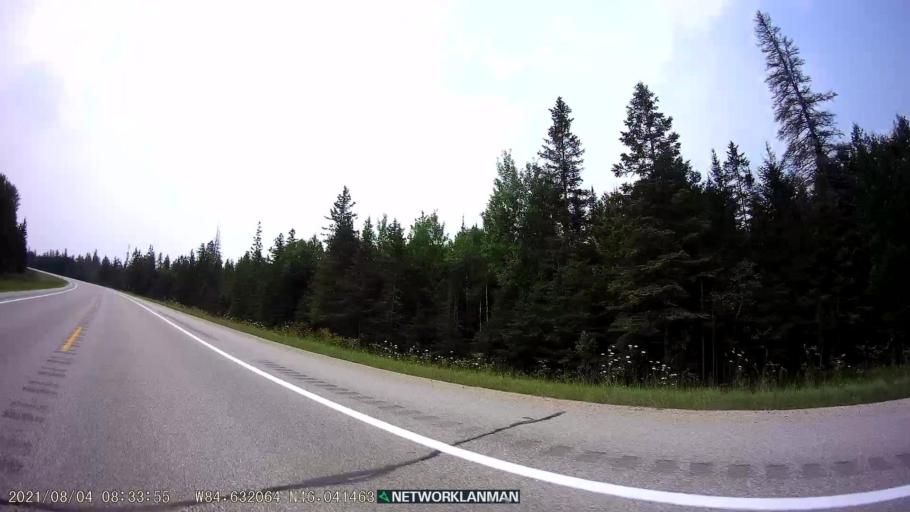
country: US
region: Michigan
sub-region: Mackinac County
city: Saint Ignace
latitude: 46.0402
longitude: -84.6266
